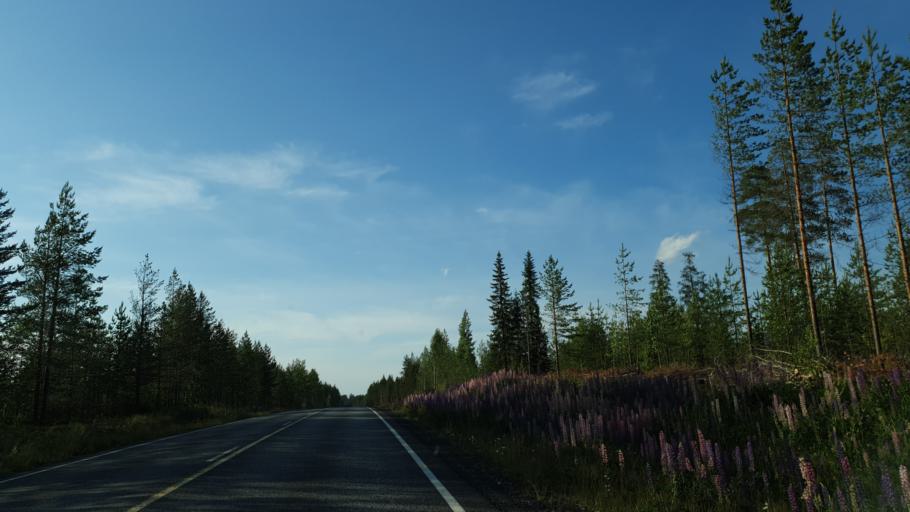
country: FI
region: Kainuu
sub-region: Kehys-Kainuu
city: Kuhmo
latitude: 64.0842
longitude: 29.4841
